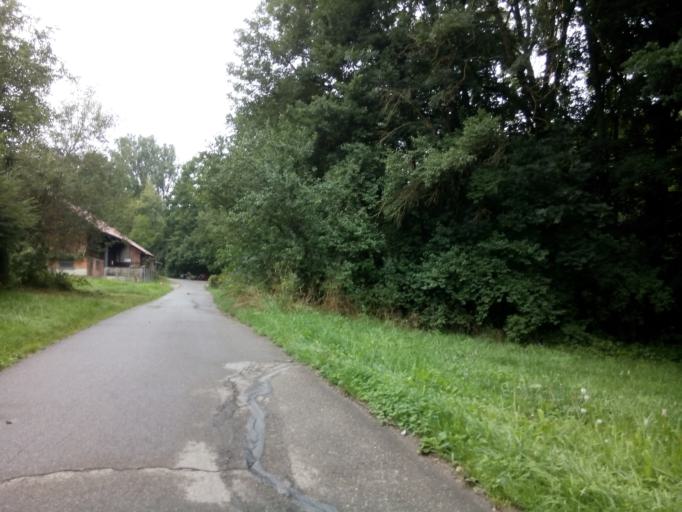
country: DE
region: Baden-Wuerttemberg
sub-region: Tuebingen Region
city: Tuebingen
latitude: 48.5325
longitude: 9.0450
